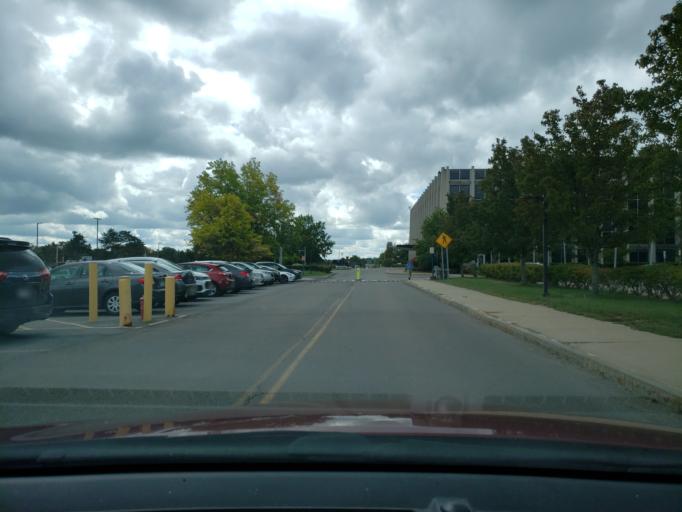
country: US
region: New York
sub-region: Monroe County
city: North Gates
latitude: 43.1530
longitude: -77.7345
